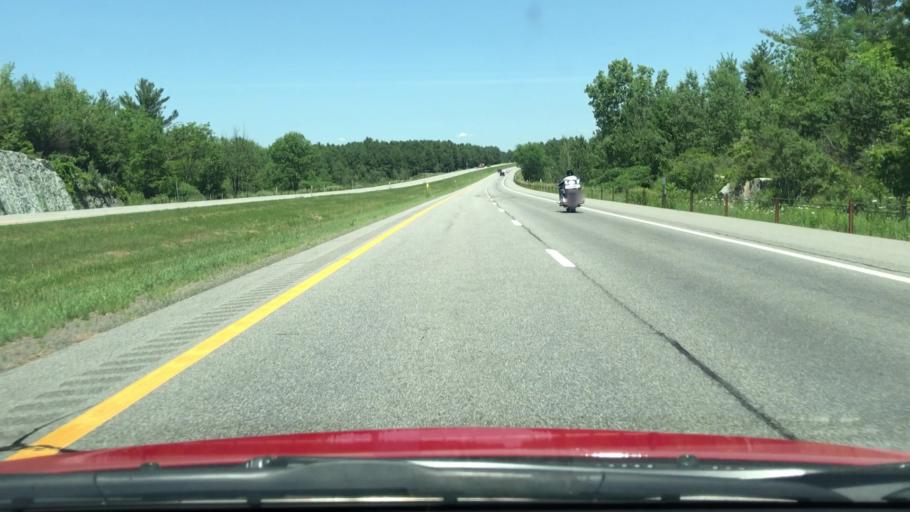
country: US
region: New York
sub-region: Essex County
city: Keeseville
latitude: 44.4757
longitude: -73.4881
